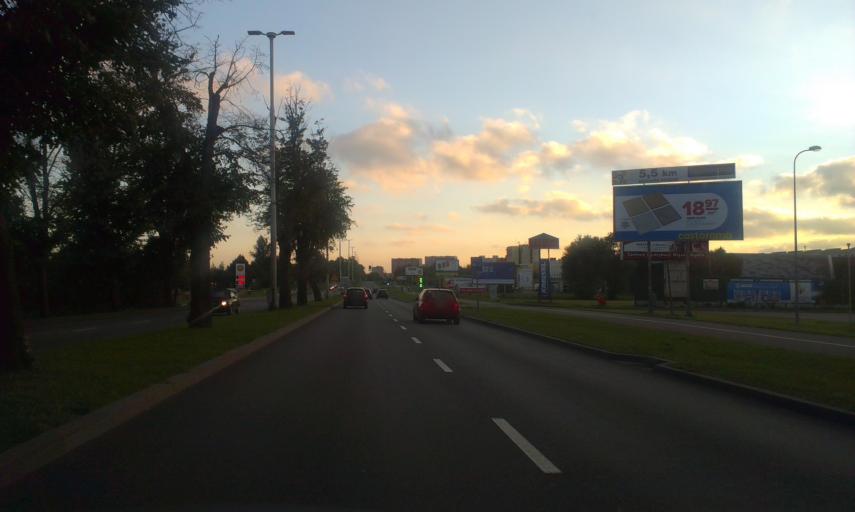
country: PL
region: West Pomeranian Voivodeship
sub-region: Koszalin
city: Koszalin
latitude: 54.2064
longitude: 16.2073
